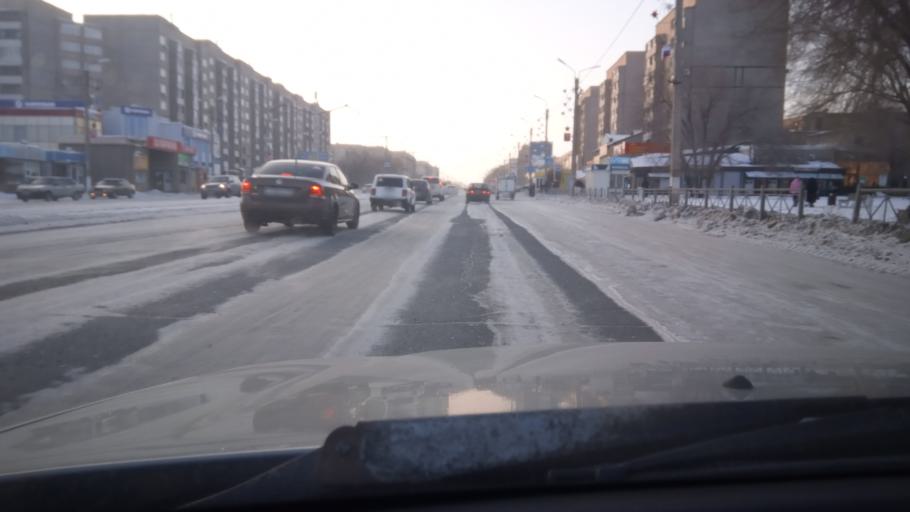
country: RU
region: Orenburg
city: Novotroitsk
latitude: 51.1917
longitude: 58.2865
